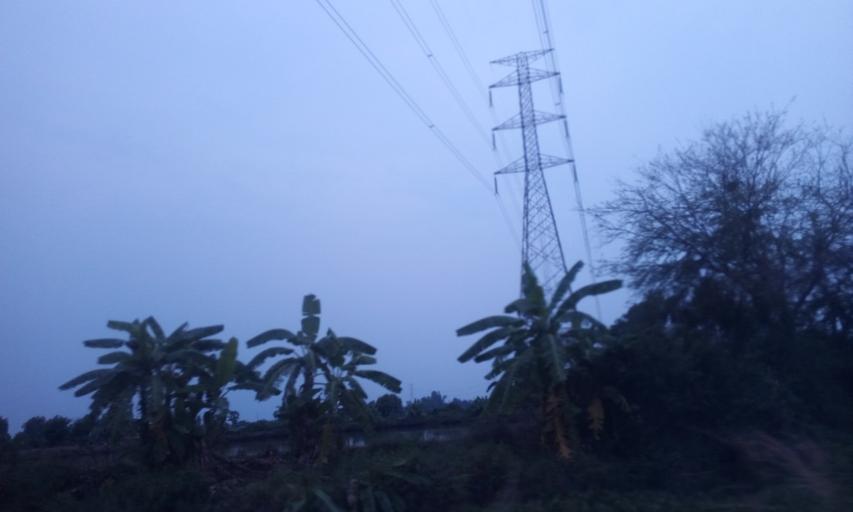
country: TH
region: Chachoengsao
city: Ban Pho
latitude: 13.5999
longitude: 101.1679
